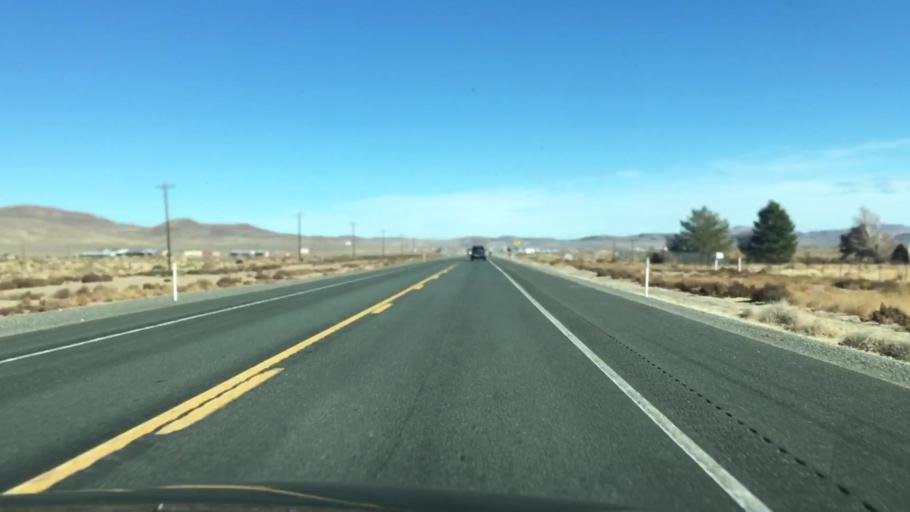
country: US
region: Nevada
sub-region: Lyon County
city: Silver Springs
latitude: 39.3975
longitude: -119.2760
